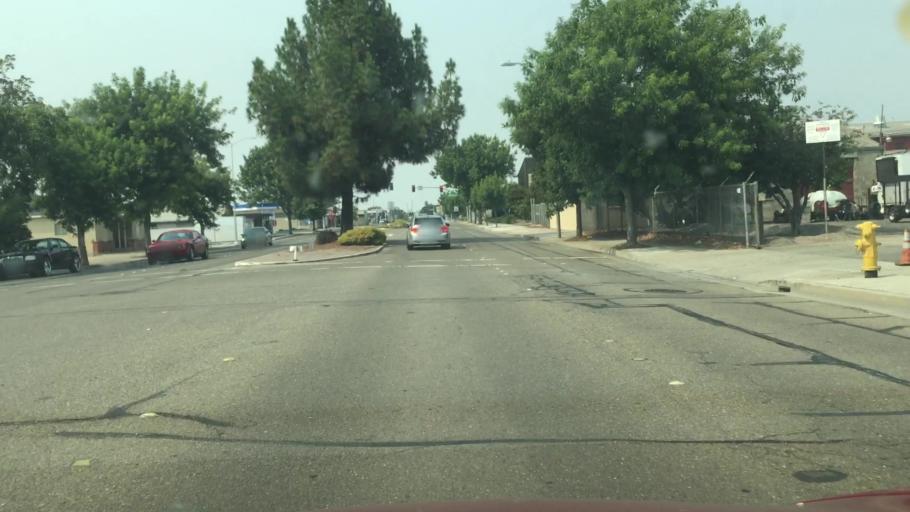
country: US
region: California
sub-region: San Joaquin County
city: Manteca
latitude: 37.7922
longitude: -121.2162
